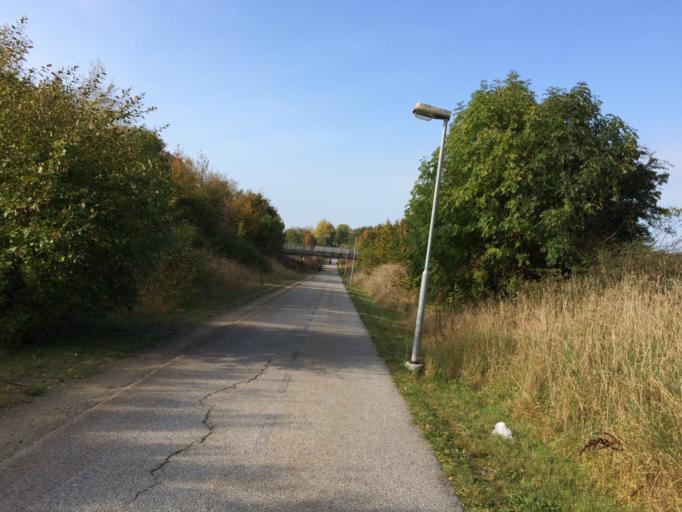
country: SE
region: Skane
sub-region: Lunds Kommun
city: Lund
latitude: 55.7100
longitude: 13.2522
